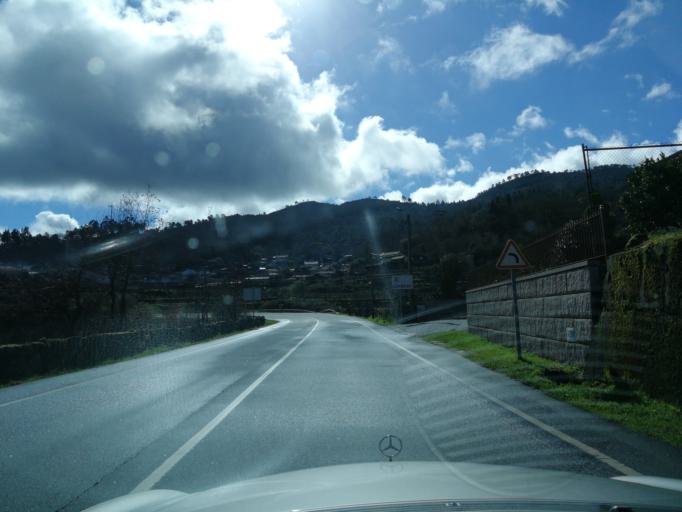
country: ES
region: Galicia
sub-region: Provincia de Ourense
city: Entrimo
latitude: 41.8667
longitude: -8.2044
